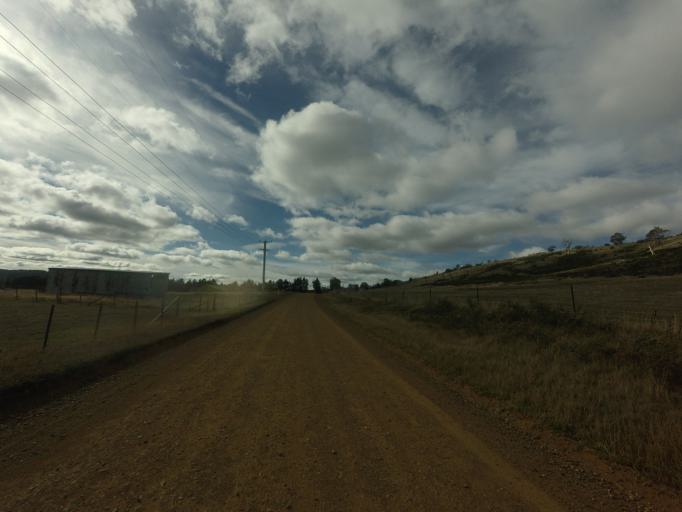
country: AU
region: Tasmania
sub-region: Brighton
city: Bridgewater
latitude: -42.4167
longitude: 147.3947
